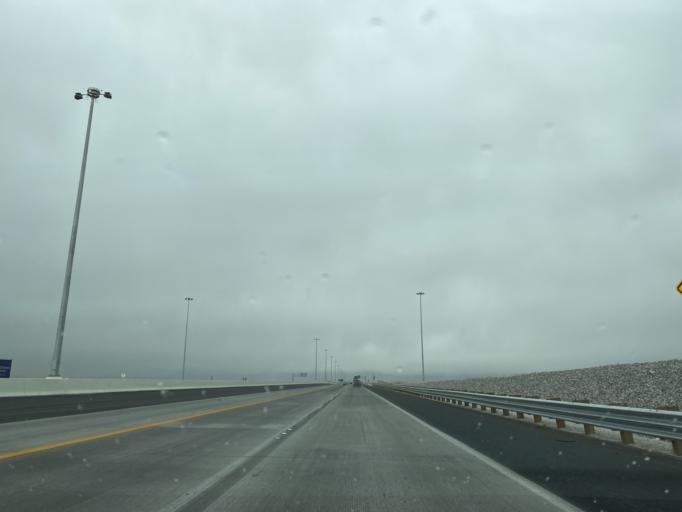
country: US
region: Nevada
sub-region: Clark County
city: Nellis Air Force Base
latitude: 36.2899
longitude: -115.0996
